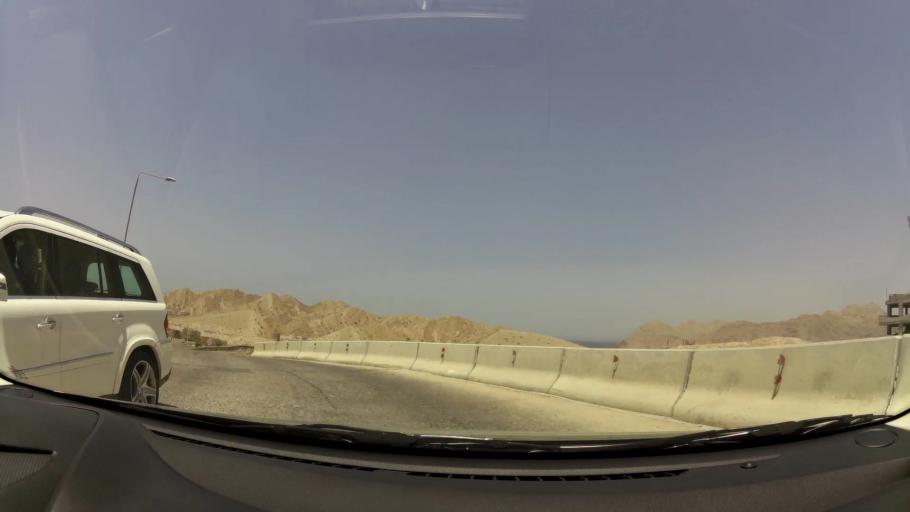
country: OM
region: Muhafazat Masqat
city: Muscat
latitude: 23.6249
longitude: 58.5025
